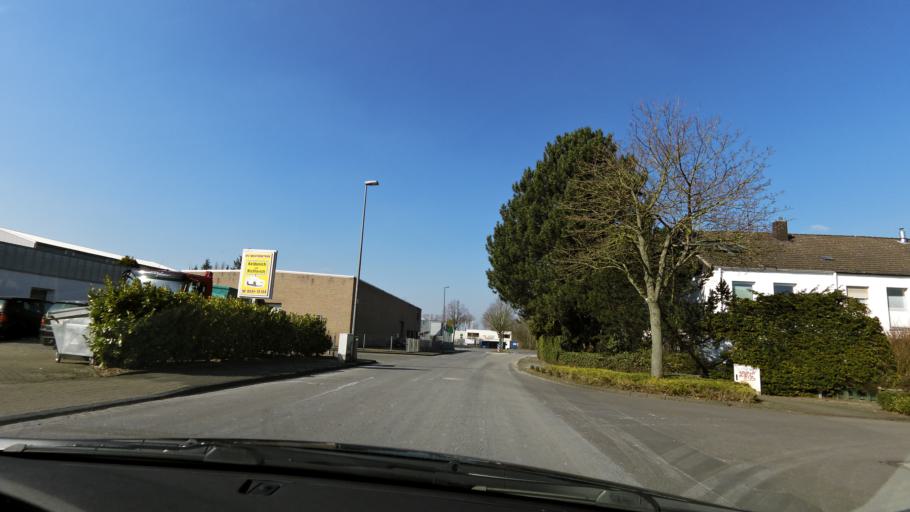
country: DE
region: North Rhine-Westphalia
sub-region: Regierungsbezirk Koln
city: Aachen
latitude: 50.8134
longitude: 6.0644
